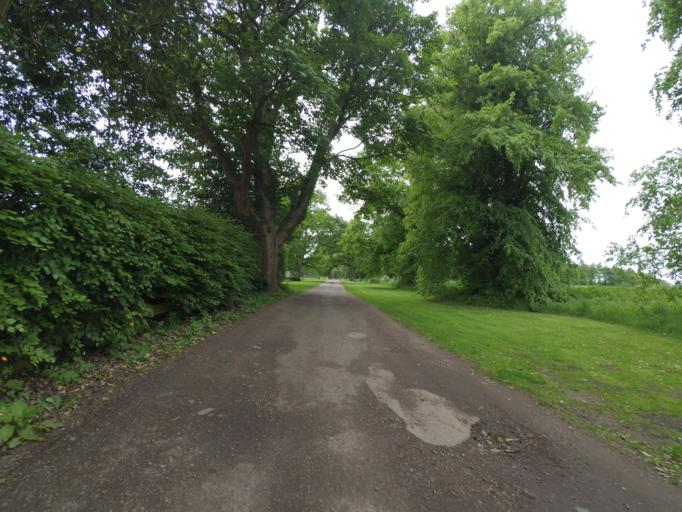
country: GB
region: Scotland
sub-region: East Lothian
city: Pencaitland
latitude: 55.9119
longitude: -2.8912
